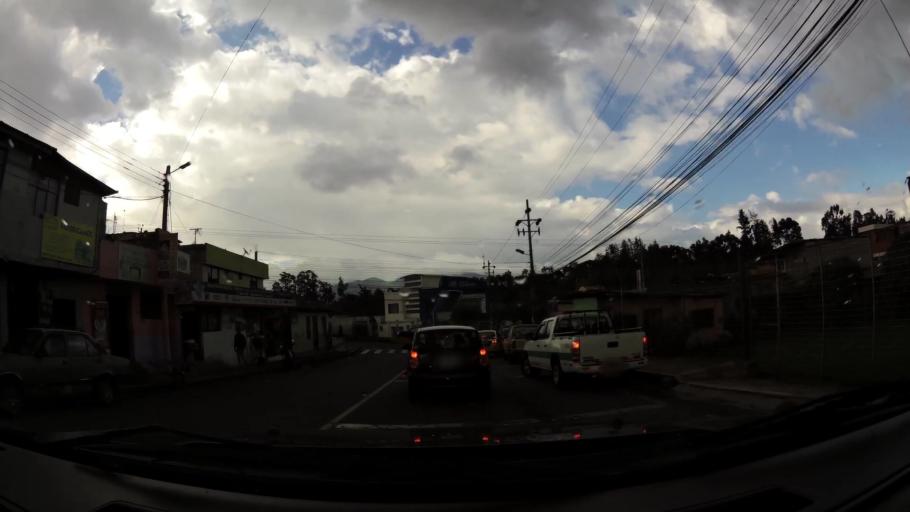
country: EC
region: Pichincha
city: Sangolqui
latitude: -0.3343
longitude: -78.4416
